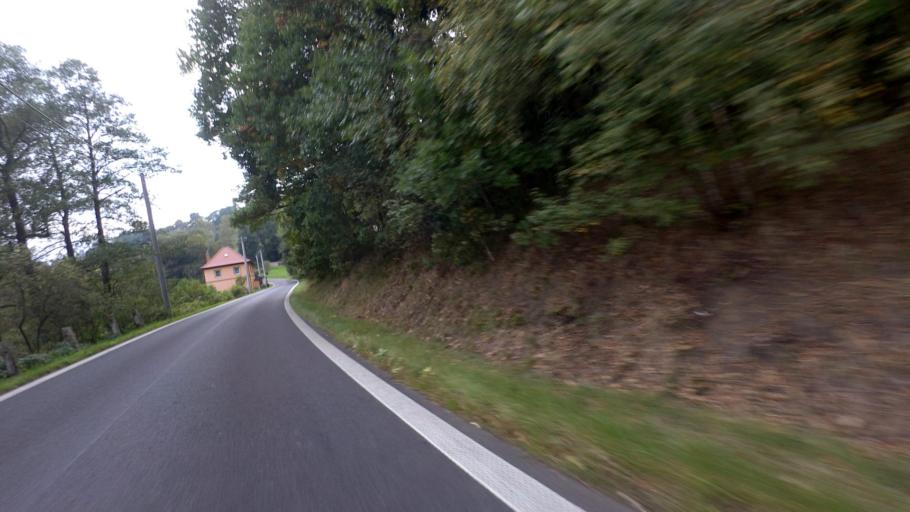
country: CZ
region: Ustecky
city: Dolni Poustevna
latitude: 51.0069
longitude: 14.2963
